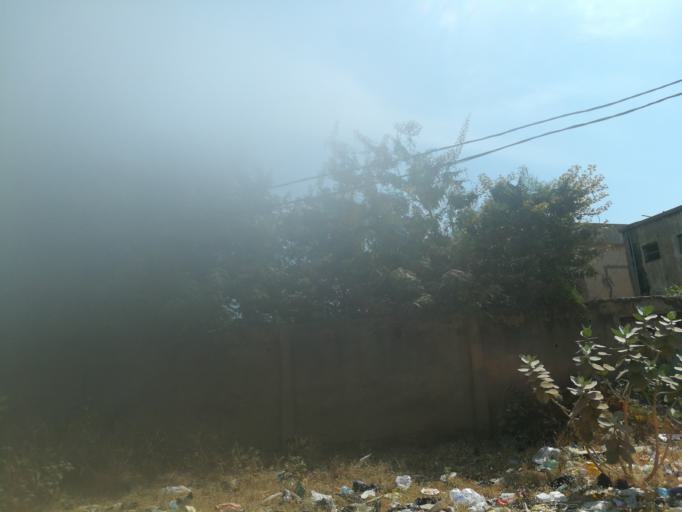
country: NG
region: Kano
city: Kano
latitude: 12.0300
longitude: 8.5149
